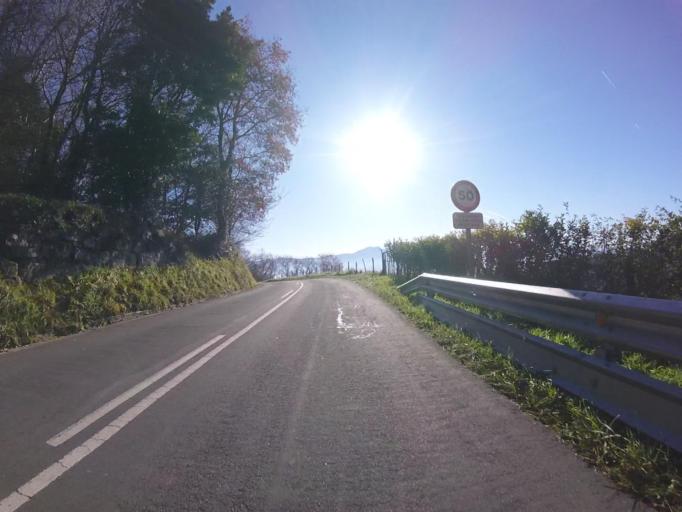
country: ES
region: Basque Country
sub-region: Provincia de Guipuzcoa
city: Fuenterrabia
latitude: 43.3698
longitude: -1.8139
